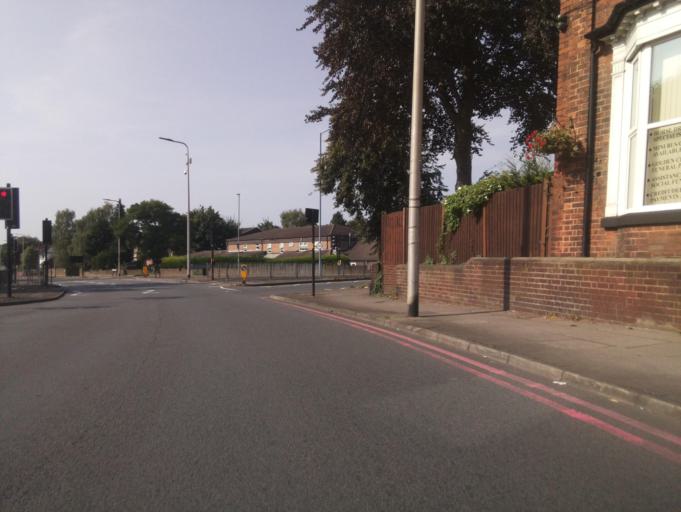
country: GB
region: England
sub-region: Sandwell
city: West Bromwich
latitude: 52.5348
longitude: -1.9853
